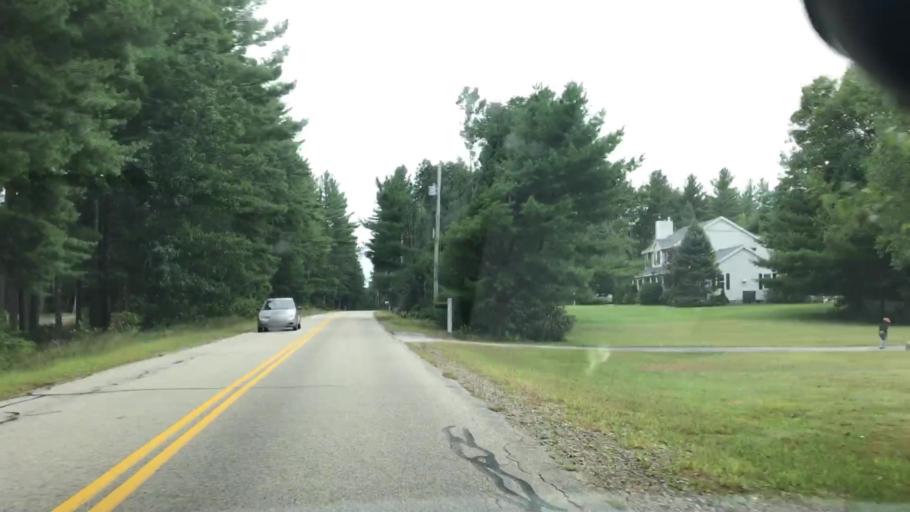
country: US
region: New Hampshire
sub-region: Hillsborough County
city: Merrimack
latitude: 42.8491
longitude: -71.5704
